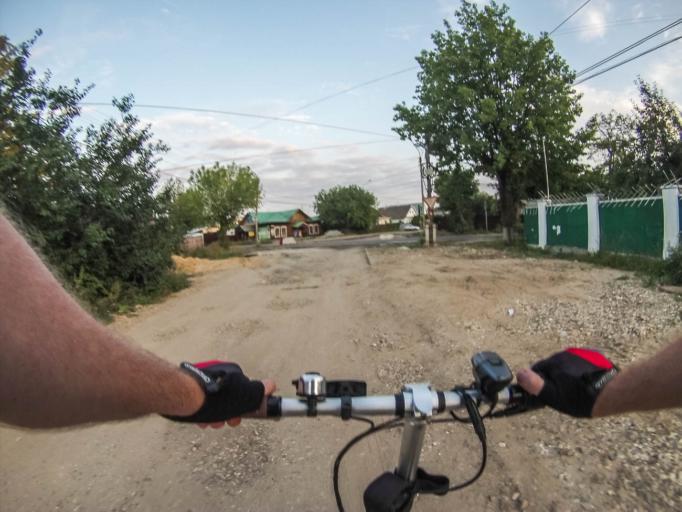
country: RU
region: Kostroma
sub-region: Kostromskoy Rayon
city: Kostroma
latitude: 57.7730
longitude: 40.9573
